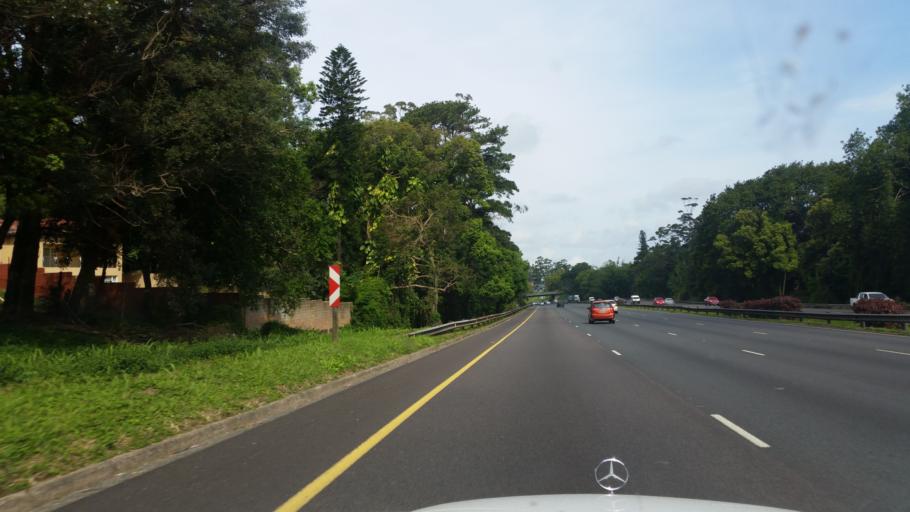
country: ZA
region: KwaZulu-Natal
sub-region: eThekwini Metropolitan Municipality
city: Berea
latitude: -29.8379
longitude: 30.9103
